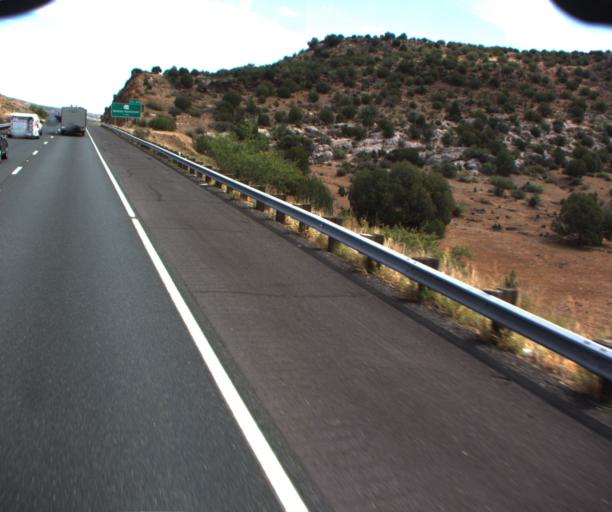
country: US
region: Arizona
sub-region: Yavapai County
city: Camp Verde
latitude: 34.4990
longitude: -112.0022
